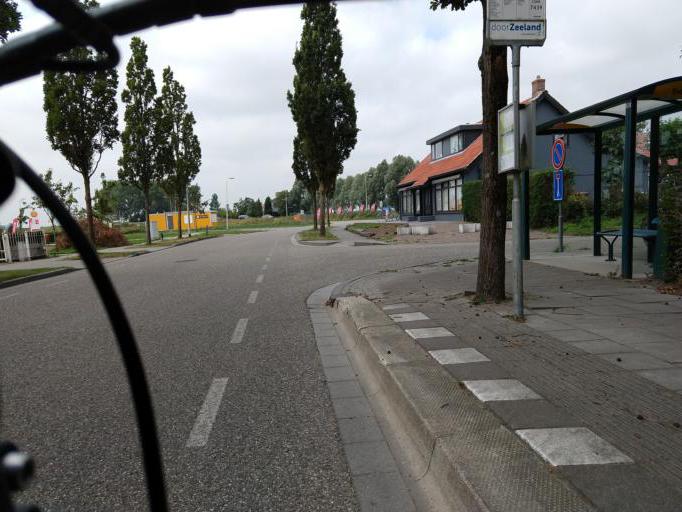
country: NL
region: Zeeland
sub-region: Schouwen-Duiveland
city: Bruinisse
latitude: 51.6528
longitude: 4.0295
